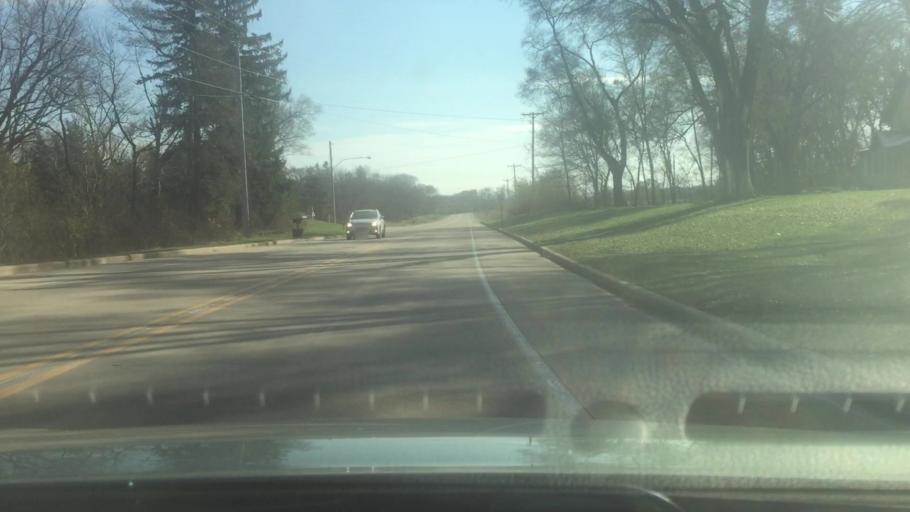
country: US
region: Wisconsin
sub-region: Jefferson County
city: Cambridge
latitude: 42.9978
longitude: -89.0020
